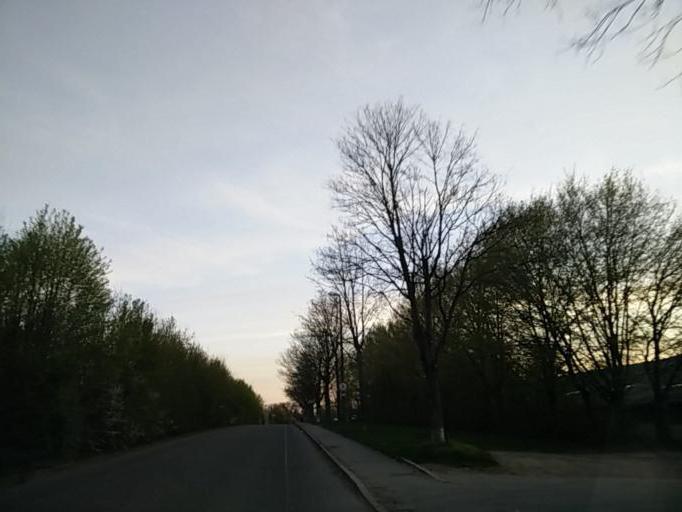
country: DE
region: Baden-Wuerttemberg
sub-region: Tuebingen Region
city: Tuebingen
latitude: 48.5481
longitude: 9.0560
